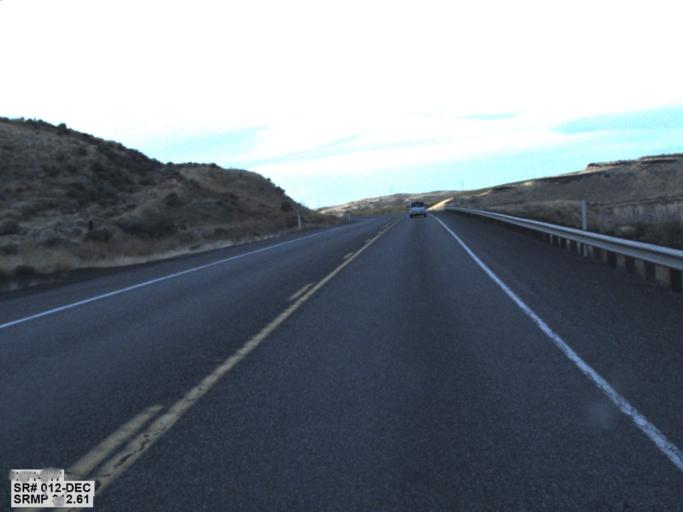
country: US
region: Washington
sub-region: Benton County
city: Finley
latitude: 46.0692
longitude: -118.8120
